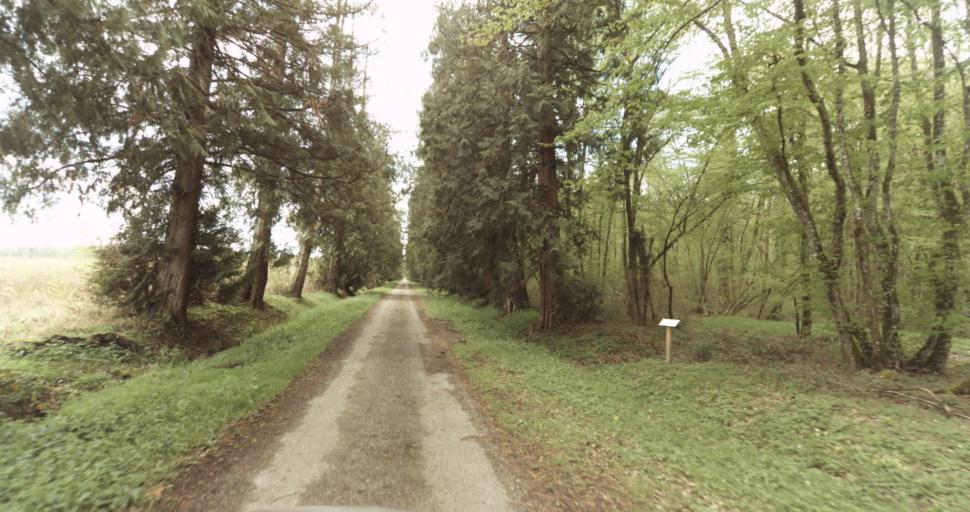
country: FR
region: Bourgogne
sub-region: Departement de la Cote-d'Or
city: Auxonne
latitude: 47.1634
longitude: 5.4232
